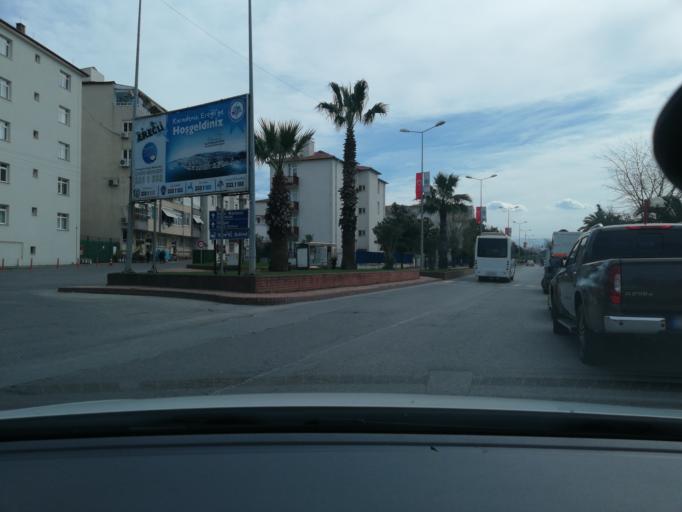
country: TR
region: Zonguldak
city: Eregli
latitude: 41.2888
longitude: 31.4102
